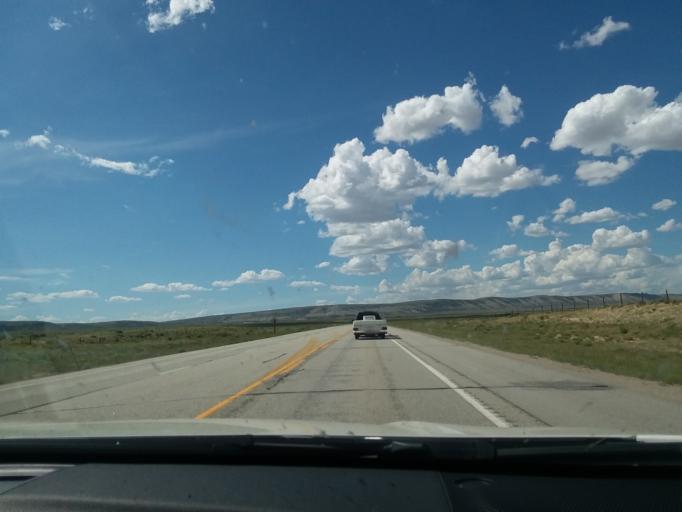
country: US
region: Wyoming
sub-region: Sweetwater County
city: North Rock Springs
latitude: 41.7129
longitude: -109.2610
